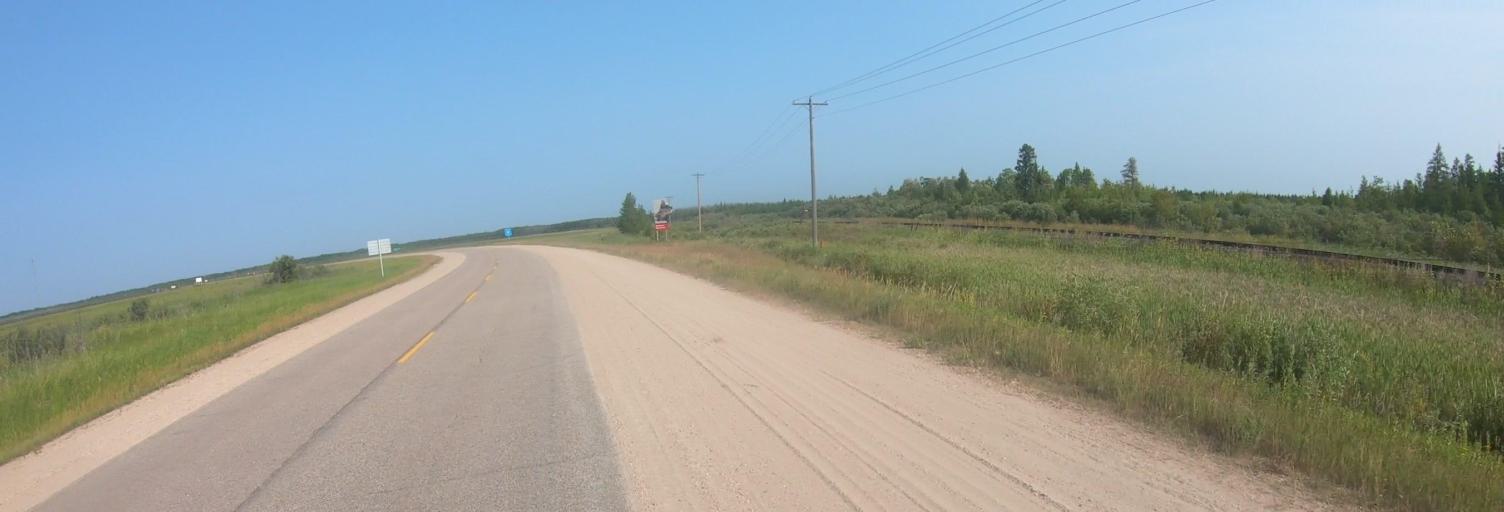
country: US
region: Minnesota
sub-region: Roseau County
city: Warroad
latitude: 49.0046
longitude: -95.3796
